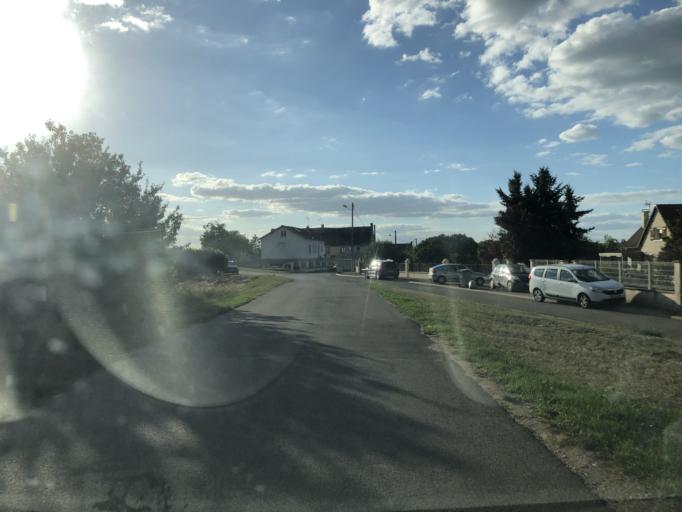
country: FR
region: Bourgogne
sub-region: Departement de l'Yonne
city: Laroche-Saint-Cydroine
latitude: 47.9502
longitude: 3.4392
